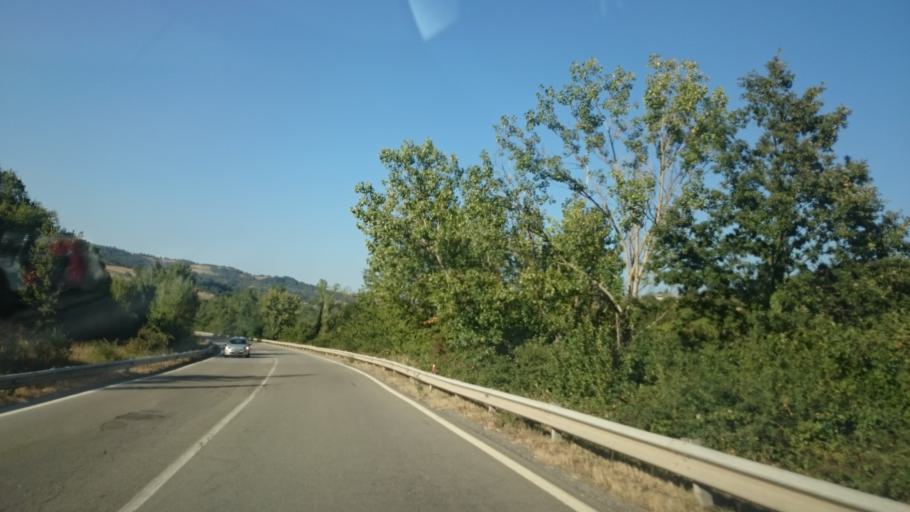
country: IT
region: Emilia-Romagna
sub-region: Provincia di Modena
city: Montefiorino
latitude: 44.4116
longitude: 10.6265
